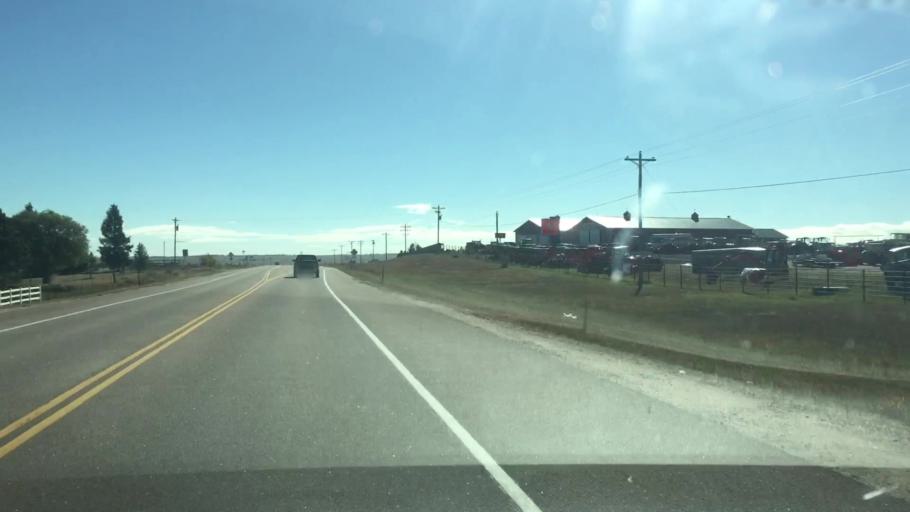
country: US
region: Colorado
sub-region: Elbert County
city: Kiowa
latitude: 39.3555
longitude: -104.5193
